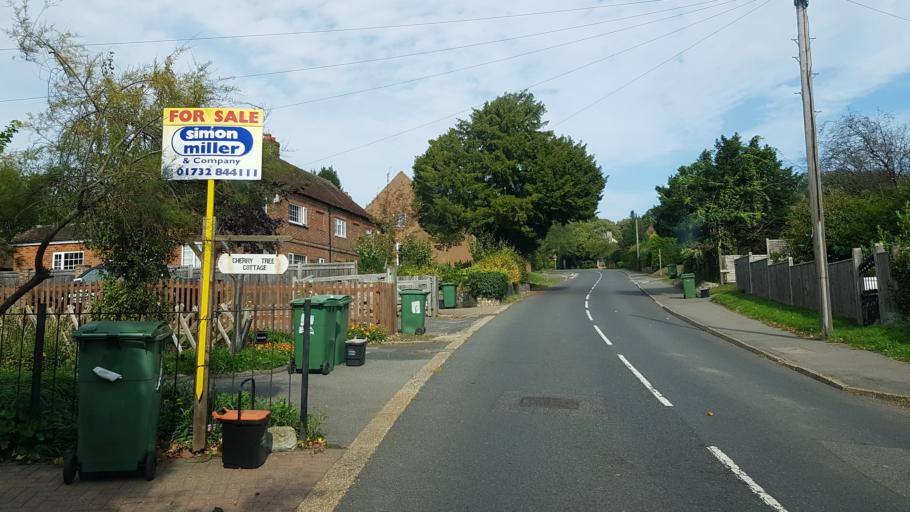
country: GB
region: England
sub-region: Kent
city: Wateringbury
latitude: 51.2558
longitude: 0.4395
